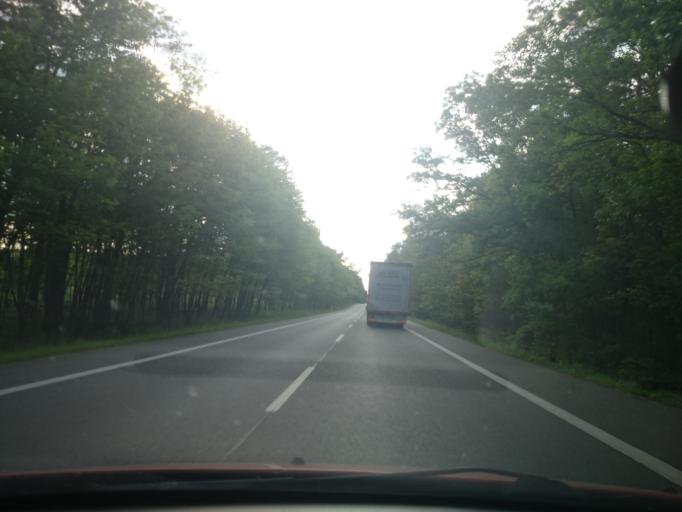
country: PL
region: Opole Voivodeship
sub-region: Powiat opolski
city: Chrzastowice
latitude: 50.6234
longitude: 18.0497
